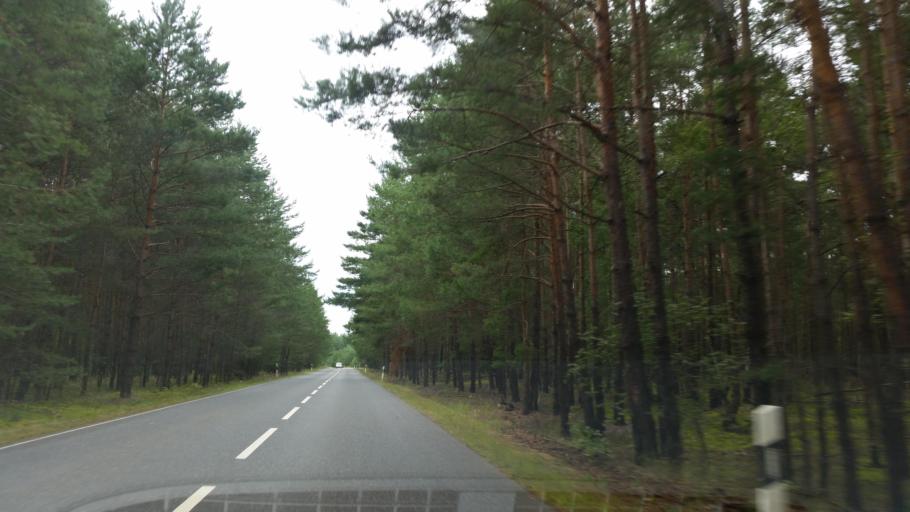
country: DE
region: Saxony
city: Klitten
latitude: 51.3946
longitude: 14.6330
